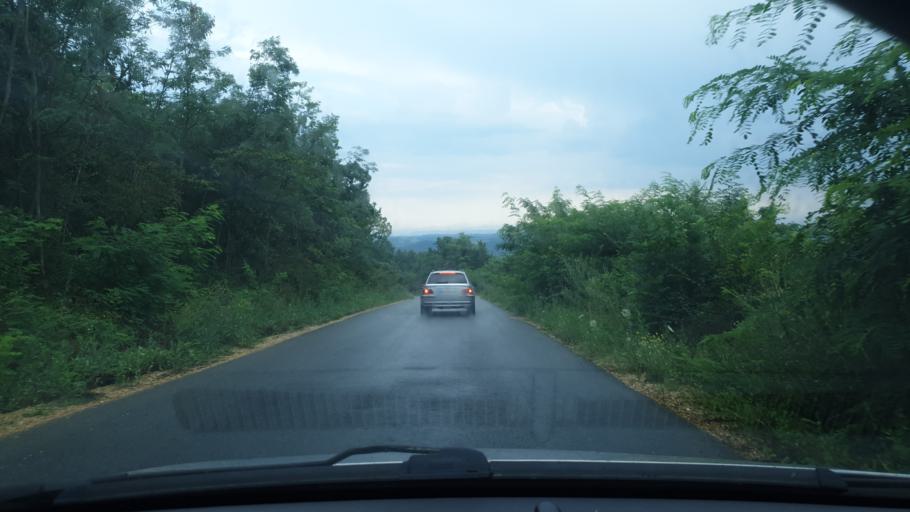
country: RS
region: Central Serbia
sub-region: Sumadijski Okrug
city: Kragujevac
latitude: 44.0532
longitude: 20.7826
